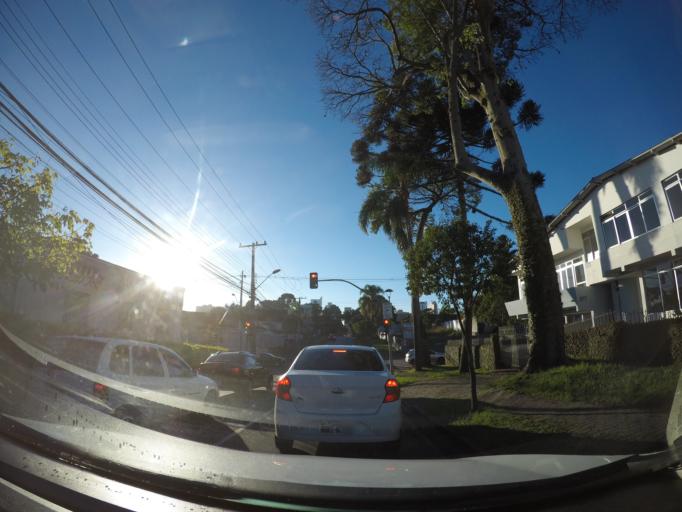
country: BR
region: Parana
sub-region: Curitiba
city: Curitiba
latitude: -25.4174
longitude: -49.2747
